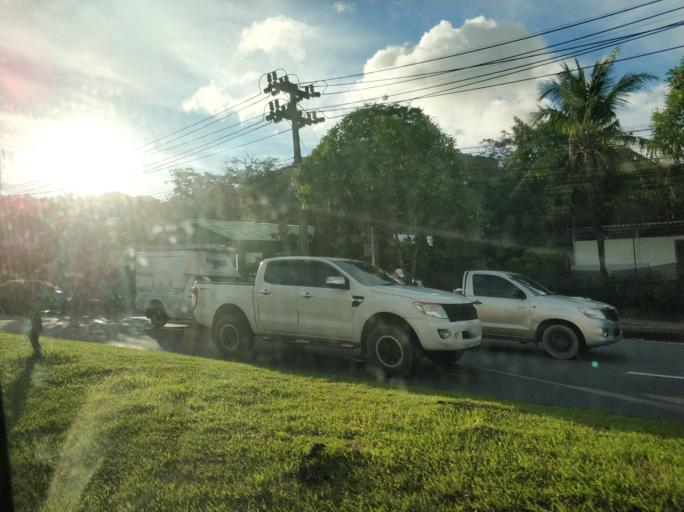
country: TH
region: Phuket
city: Kathu
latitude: 7.9098
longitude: 98.3325
